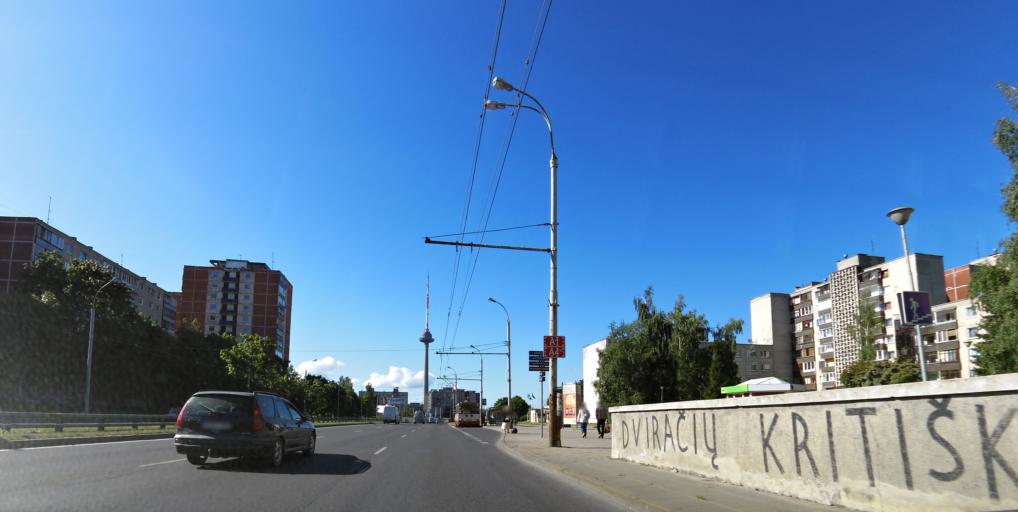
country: LT
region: Vilnius County
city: Justiniskes
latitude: 54.6970
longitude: 25.2203
